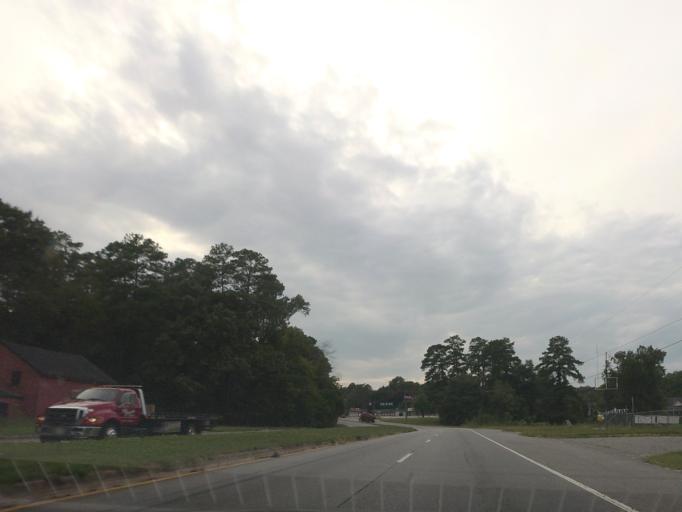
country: US
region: Georgia
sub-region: Bibb County
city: Macon
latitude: 32.8483
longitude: -83.5999
